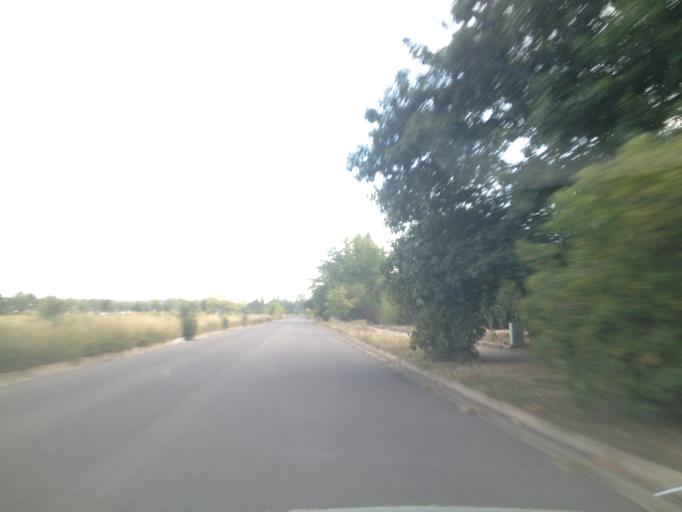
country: US
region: Colorado
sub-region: Boulder County
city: Boulder
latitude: 39.9956
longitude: -105.2244
